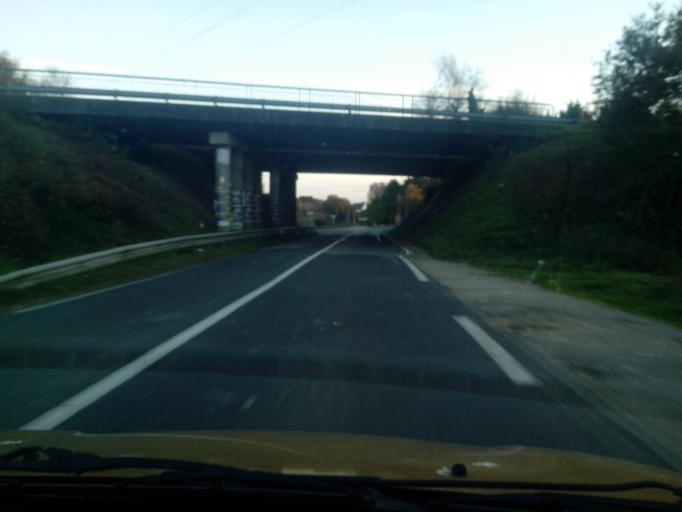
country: FR
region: Brittany
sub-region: Departement du Morbihan
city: Branderion
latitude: 47.8156
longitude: -3.2220
